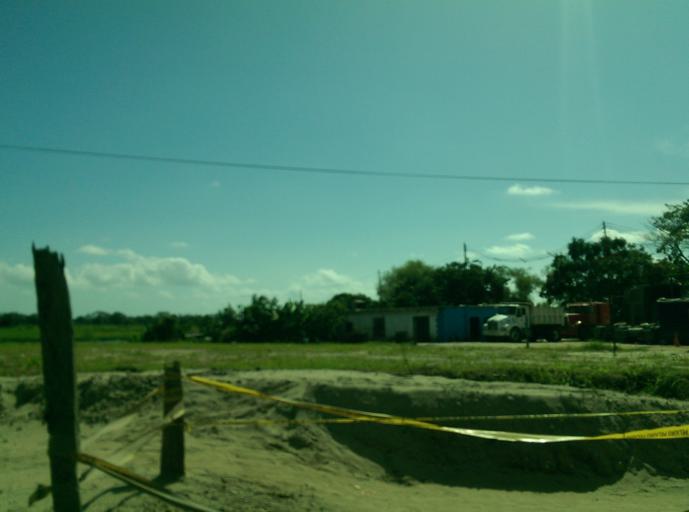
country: MX
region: Tabasco
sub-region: Centro
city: Anacleto Canabal 2da. Seccion
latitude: 17.9846
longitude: -93.0013
